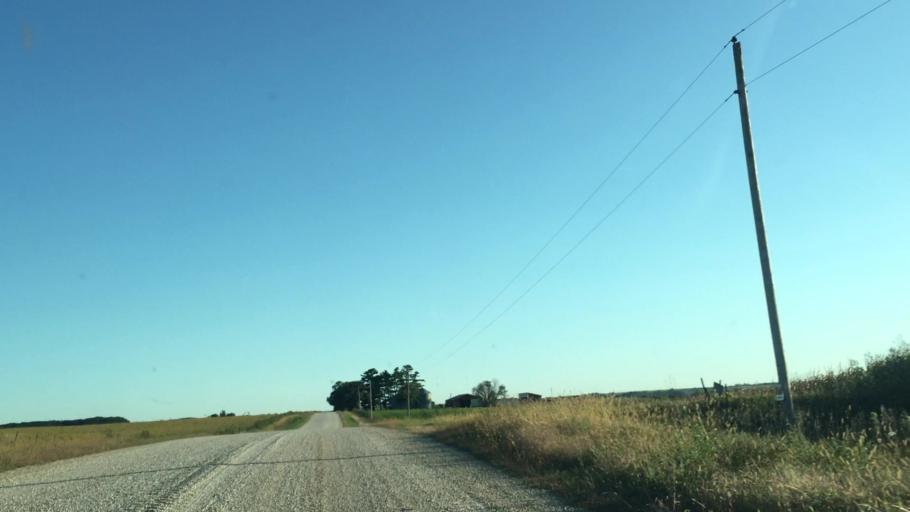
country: US
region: Minnesota
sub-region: Fillmore County
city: Preston
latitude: 43.8121
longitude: -92.0396
